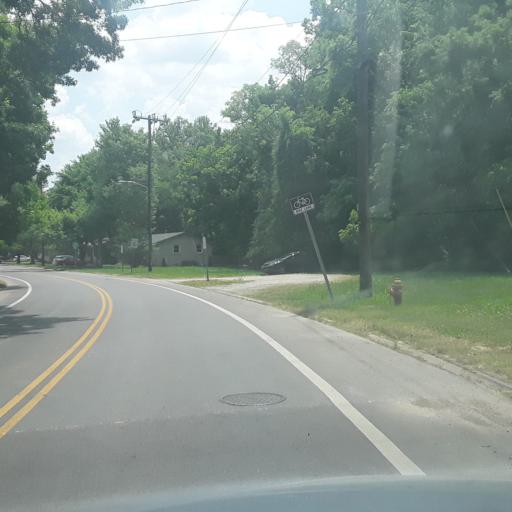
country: US
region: Tennessee
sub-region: Williamson County
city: Brentwood Estates
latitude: 36.0504
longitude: -86.6974
